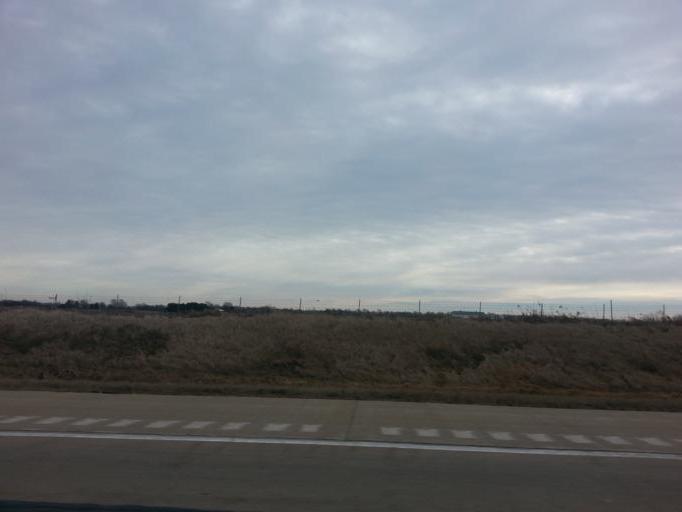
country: US
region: Illinois
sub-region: Woodford County
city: El Paso
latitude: 40.7572
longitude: -89.0343
